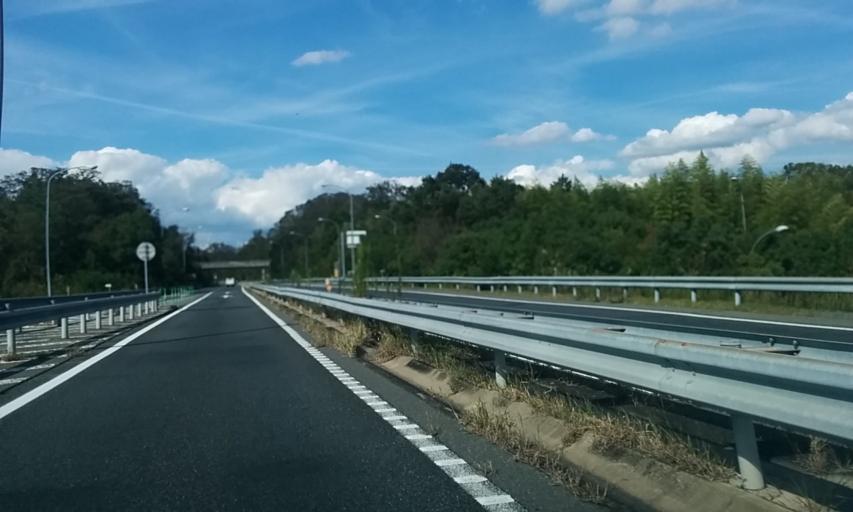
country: JP
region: Kyoto
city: Tanabe
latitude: 34.7770
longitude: 135.7733
